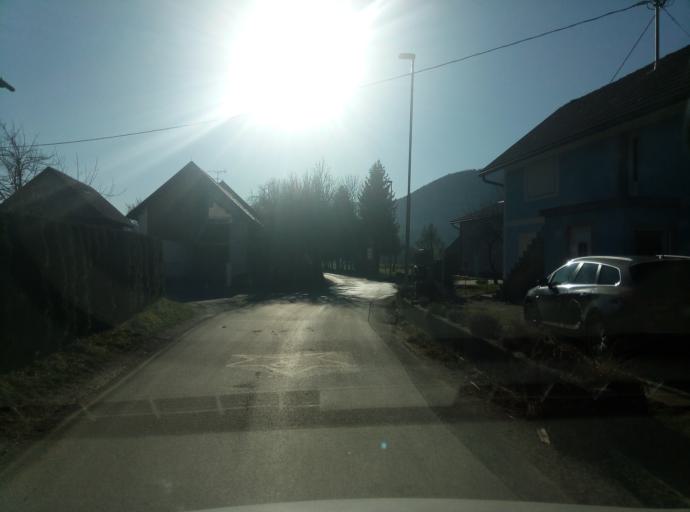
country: SI
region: Cerknica
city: Cerknica
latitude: 45.7761
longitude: 14.3579
